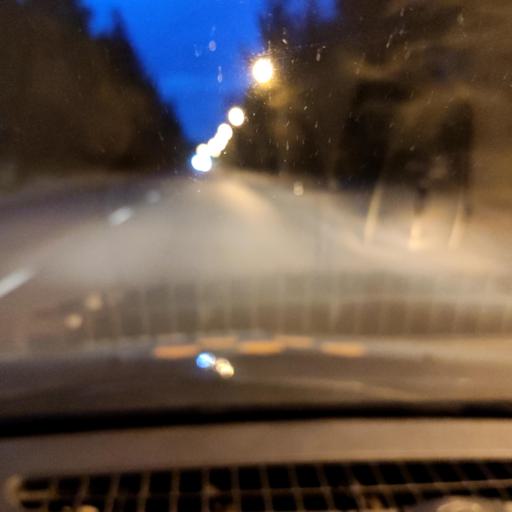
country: RU
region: Voronezj
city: Pridonskoy
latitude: 51.6863
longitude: 39.1001
